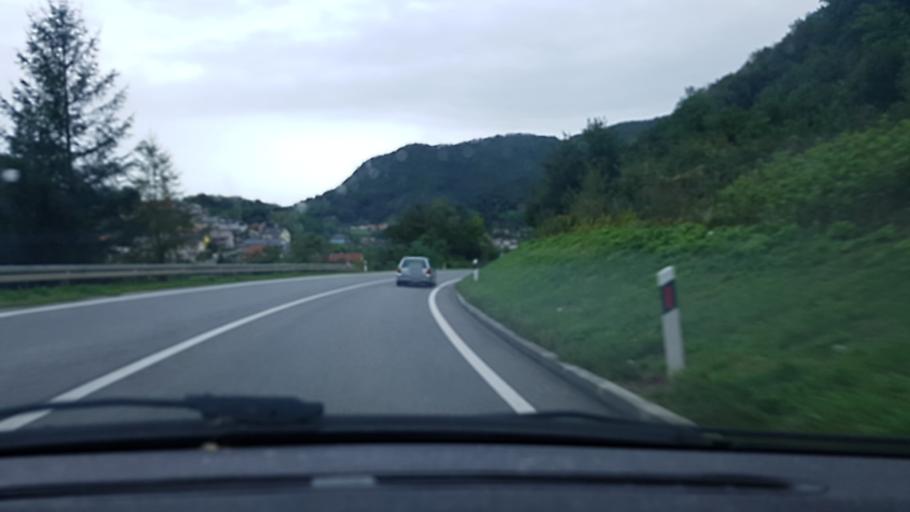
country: HR
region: Krapinsko-Zagorska
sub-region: Grad Krapina
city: Krapina
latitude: 46.1701
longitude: 15.8646
